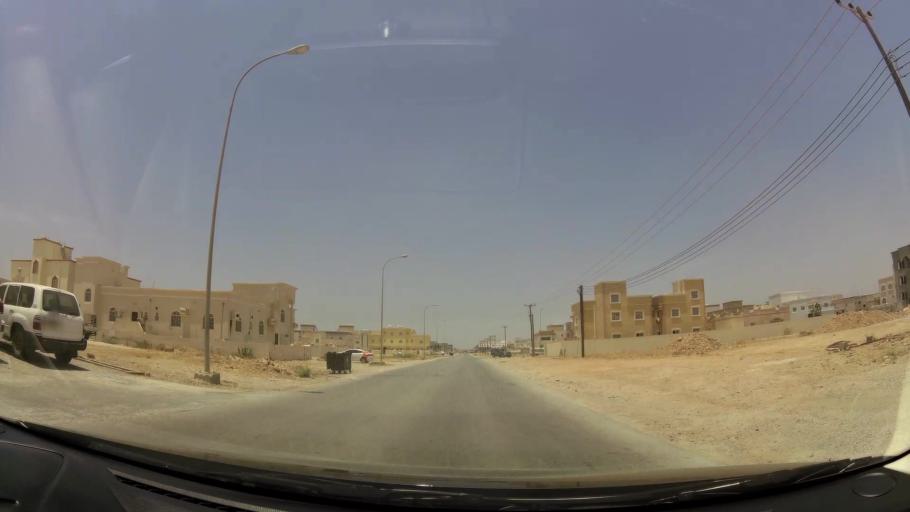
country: OM
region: Zufar
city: Salalah
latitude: 17.0959
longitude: 54.1549
